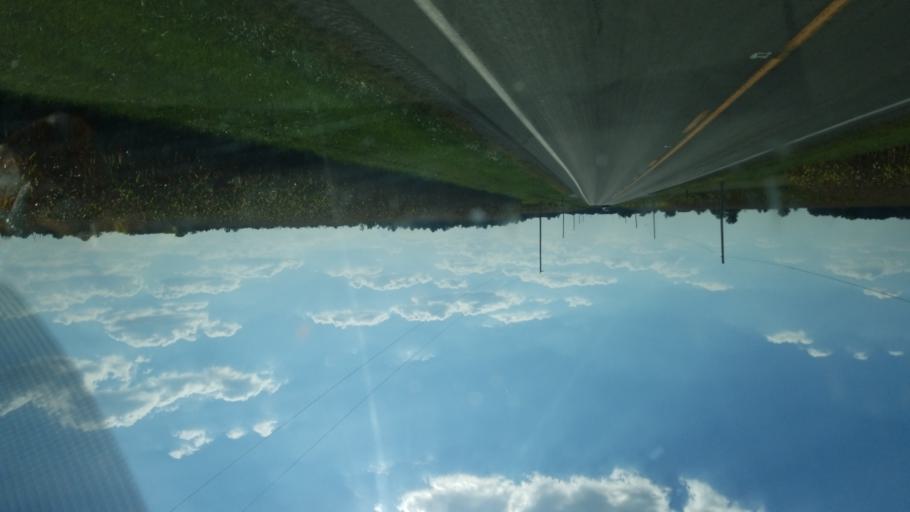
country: US
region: Ohio
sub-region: Wyandot County
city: Upper Sandusky
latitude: 40.7347
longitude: -83.3702
